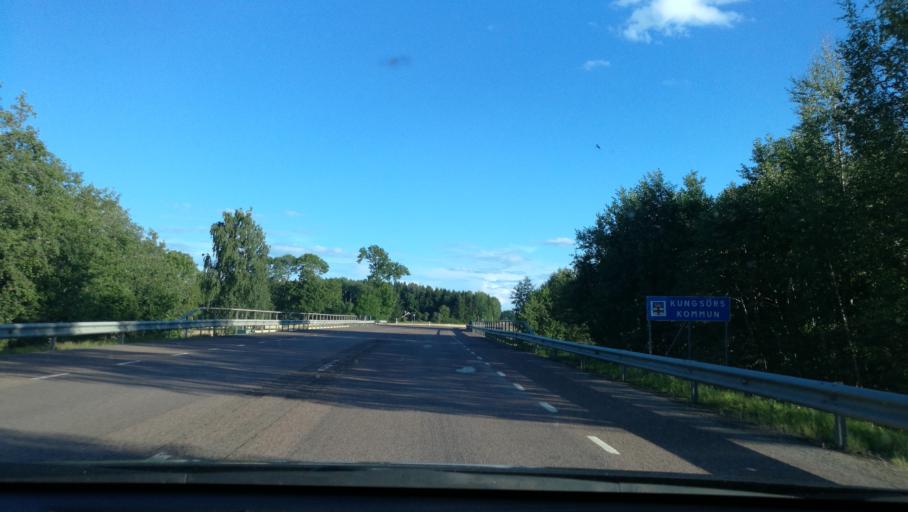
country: SE
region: Vaestmanland
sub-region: Kopings Kommun
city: Koping
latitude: 59.4775
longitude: 15.9895
